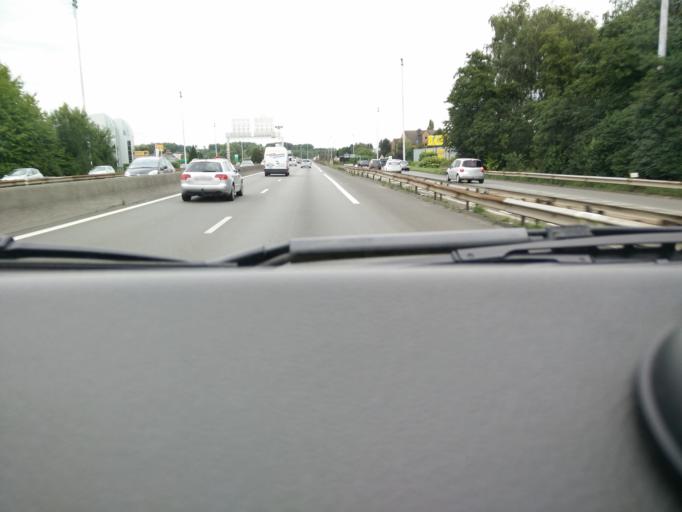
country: FR
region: Nord-Pas-de-Calais
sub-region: Departement du Nord
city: Mons-en-Baroeul
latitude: 50.6401
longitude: 3.1436
